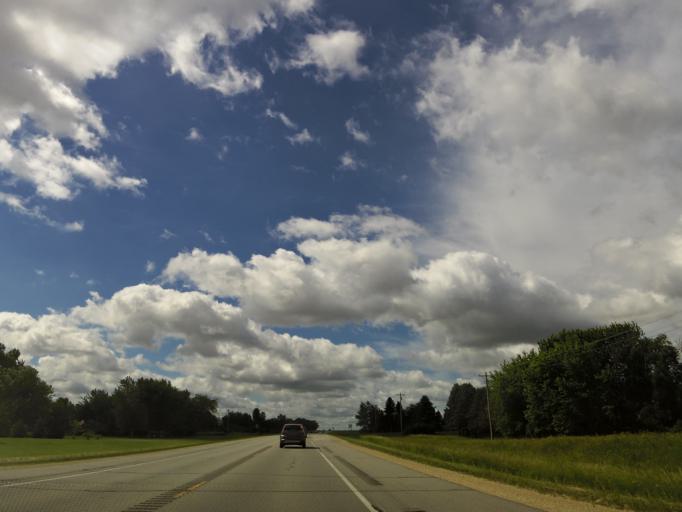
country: US
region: Minnesota
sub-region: Olmsted County
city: Stewartville
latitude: 43.8214
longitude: -92.4892
